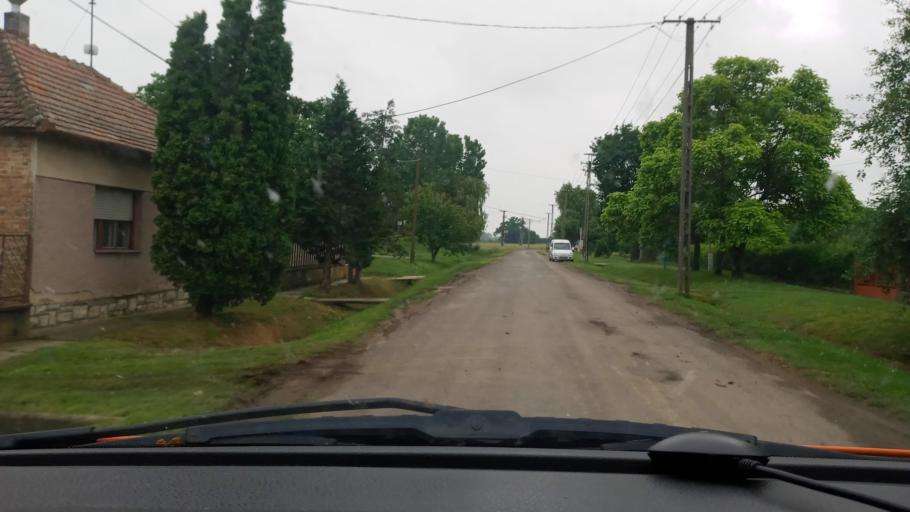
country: HU
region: Baranya
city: Szentlorinc
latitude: 46.0520
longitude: 17.9672
